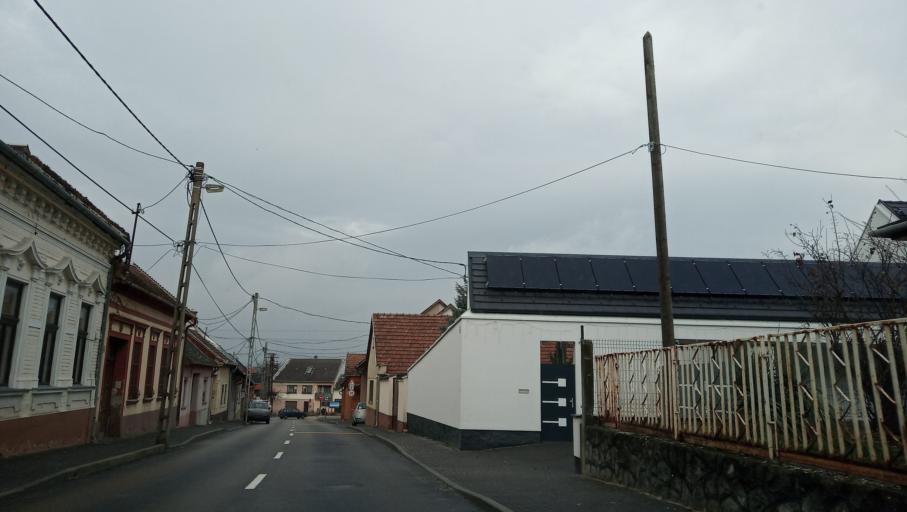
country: HU
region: Komarom-Esztergom
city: Esztergom
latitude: 47.8021
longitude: 18.7401
